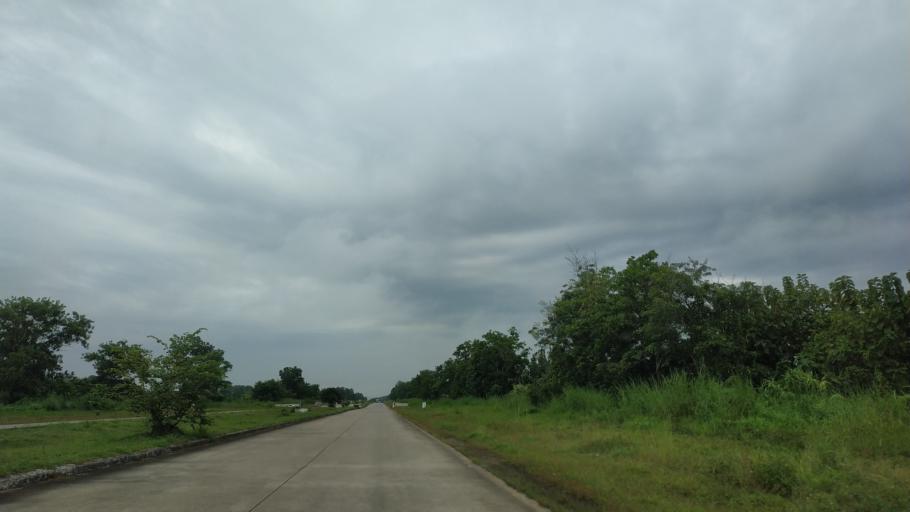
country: MM
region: Bago
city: Thanatpin
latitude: 17.3584
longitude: 96.2601
